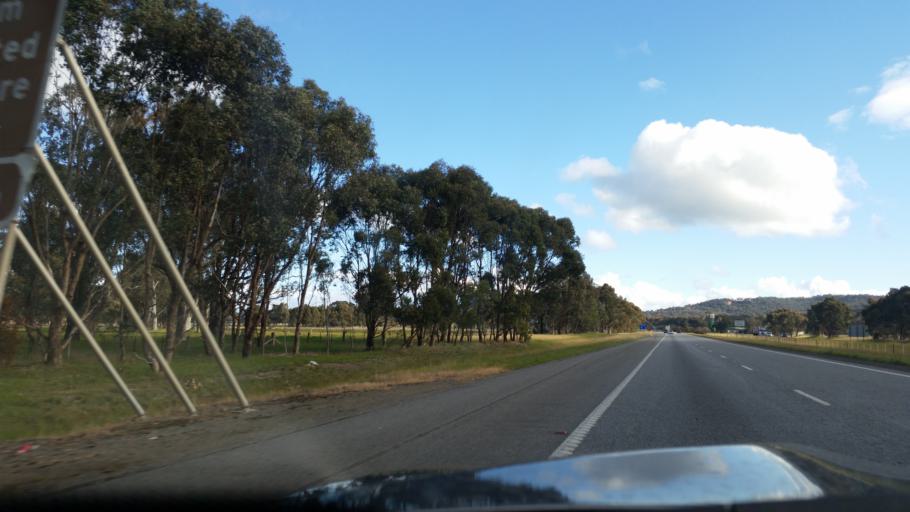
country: AU
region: Victoria
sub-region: Wangaratta
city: Wangaratta
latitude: -36.4339
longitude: 146.2545
